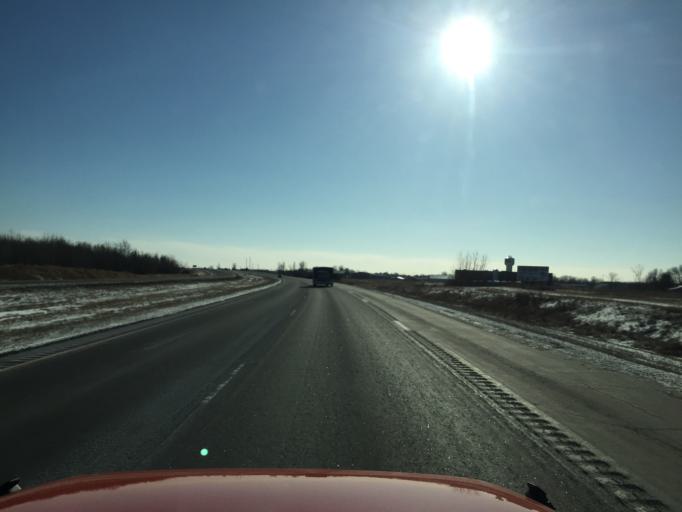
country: US
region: Minnesota
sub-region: Mille Lacs County
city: Milaca
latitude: 45.7703
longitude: -93.6455
